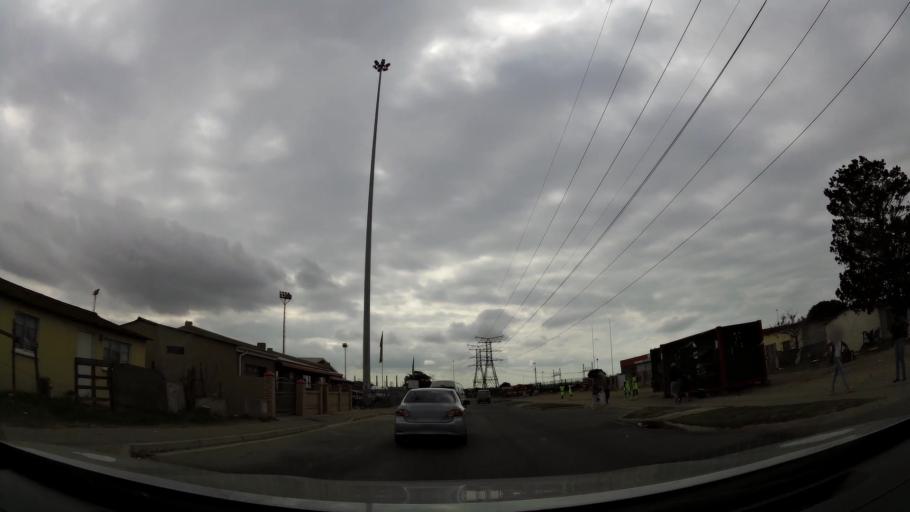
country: ZA
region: Eastern Cape
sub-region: Nelson Mandela Bay Metropolitan Municipality
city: Port Elizabeth
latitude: -33.8863
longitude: 25.5956
